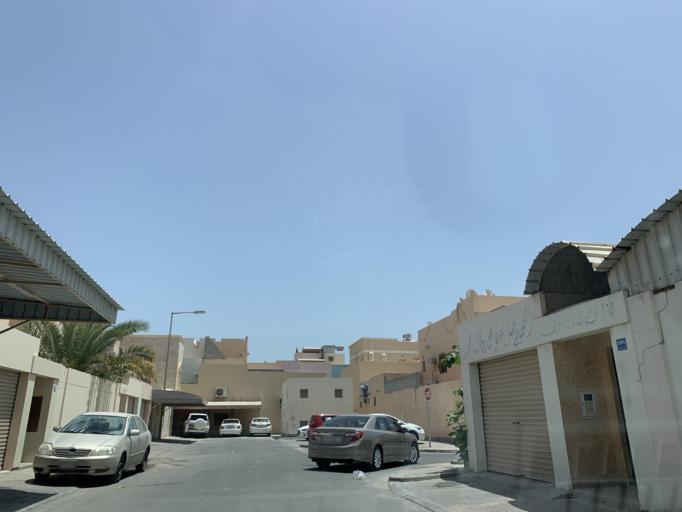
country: BH
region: Northern
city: Sitrah
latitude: 26.1422
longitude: 50.5923
